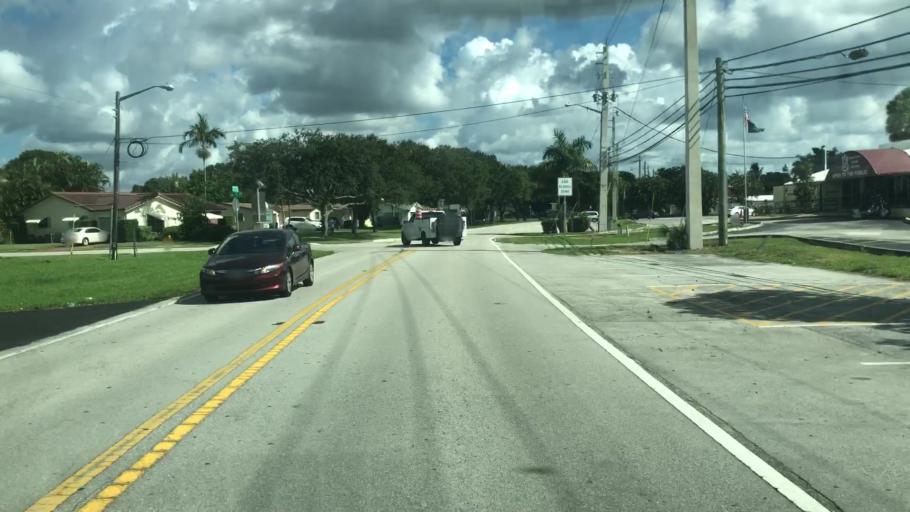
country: US
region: Florida
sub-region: Broward County
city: Cooper City
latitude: 26.0586
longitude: -80.2705
